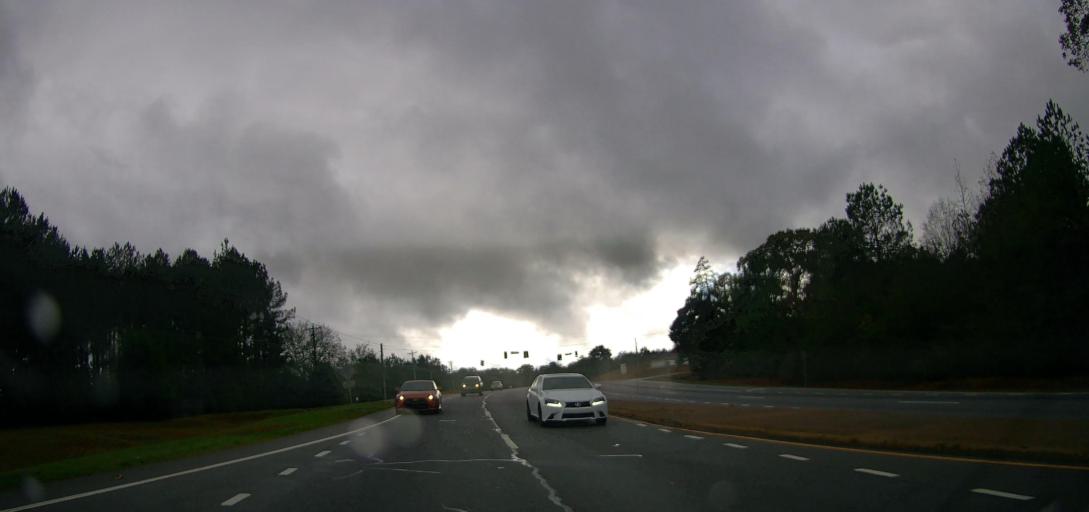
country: US
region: Georgia
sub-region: Oconee County
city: Watkinsville
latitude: 33.9039
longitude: -83.4050
